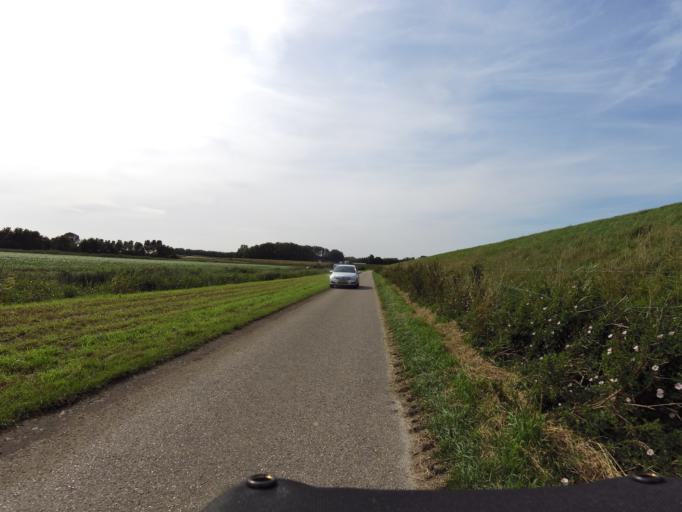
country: NL
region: South Holland
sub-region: Gemeente Goeree-Overflakkee
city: Dirksland
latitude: 51.7861
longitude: 4.1215
